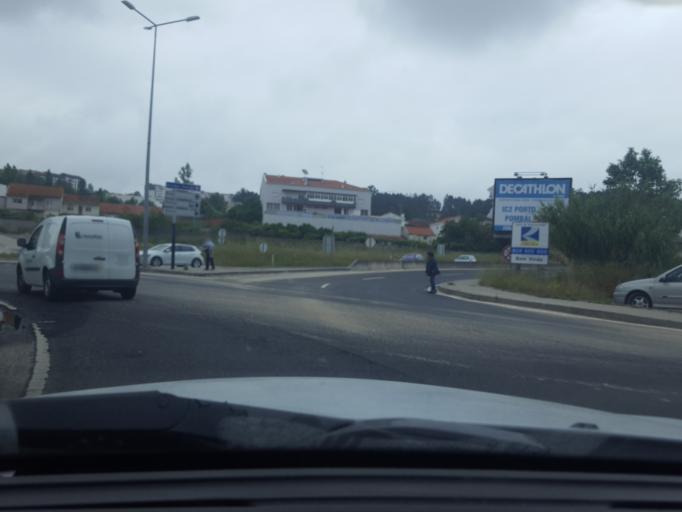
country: PT
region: Leiria
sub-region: Leiria
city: Leiria
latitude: 39.7414
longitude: -8.7927
